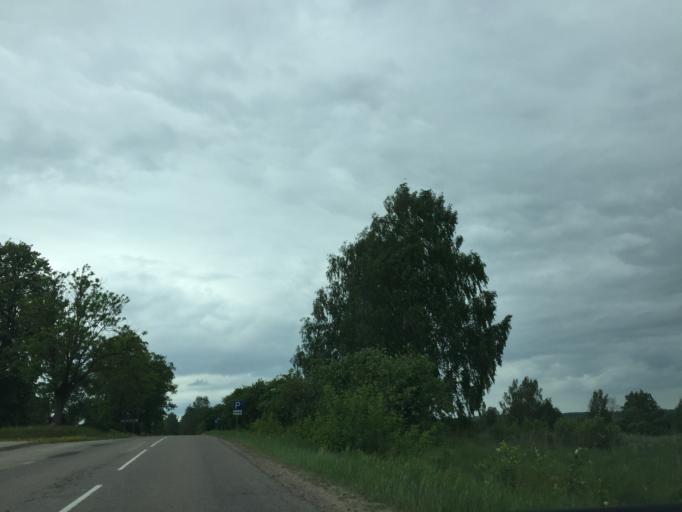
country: LV
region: Preilu Rajons
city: Preili
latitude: 56.0572
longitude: 26.7776
